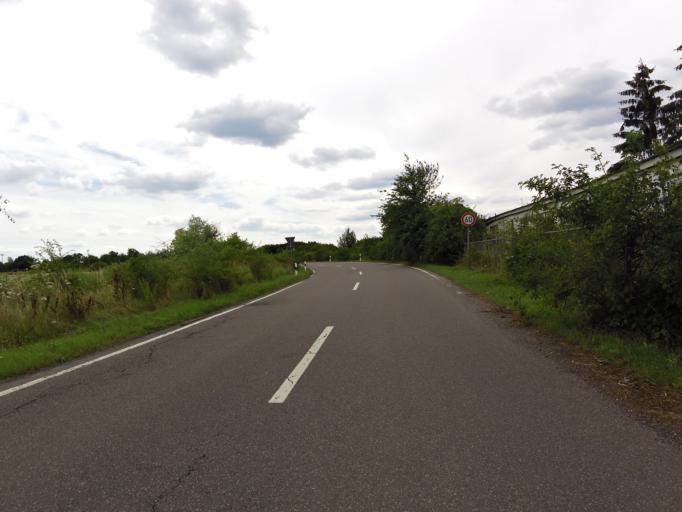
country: DE
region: Saxony
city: Rackwitz
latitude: 51.4207
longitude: 12.3803
